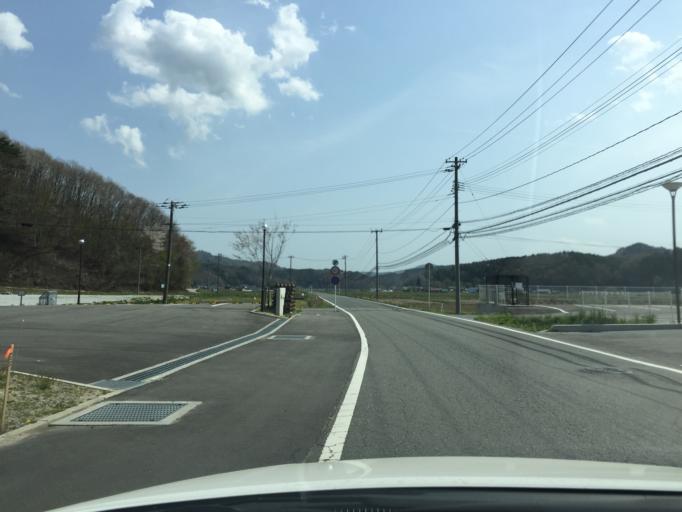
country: JP
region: Fukushima
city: Namie
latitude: 37.3255
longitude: 140.8347
